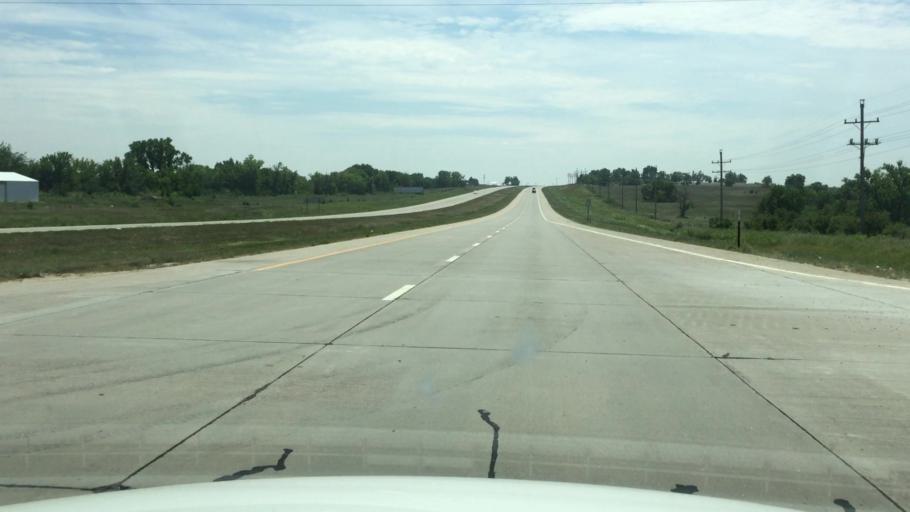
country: US
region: Kansas
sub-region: Jackson County
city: Holton
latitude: 39.2887
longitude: -95.7195
